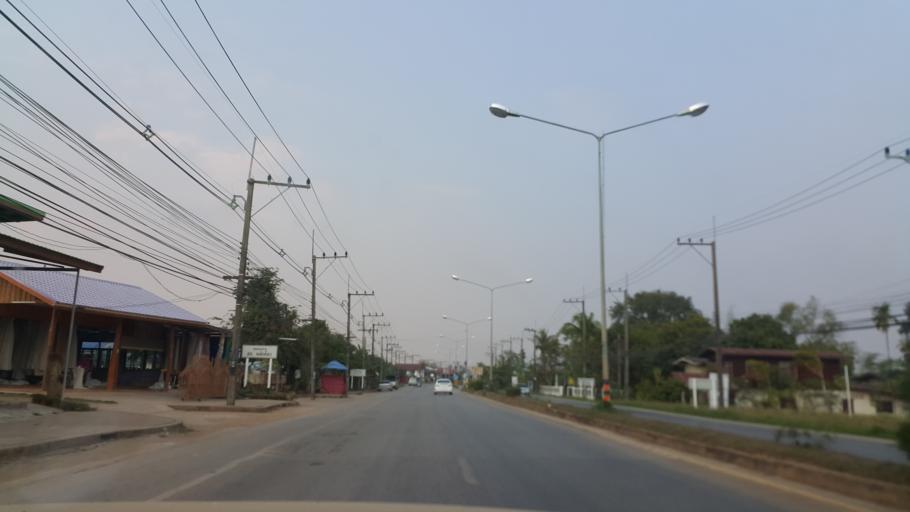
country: TH
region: Nakhon Phanom
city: That Phanom
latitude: 16.9698
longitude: 104.7273
